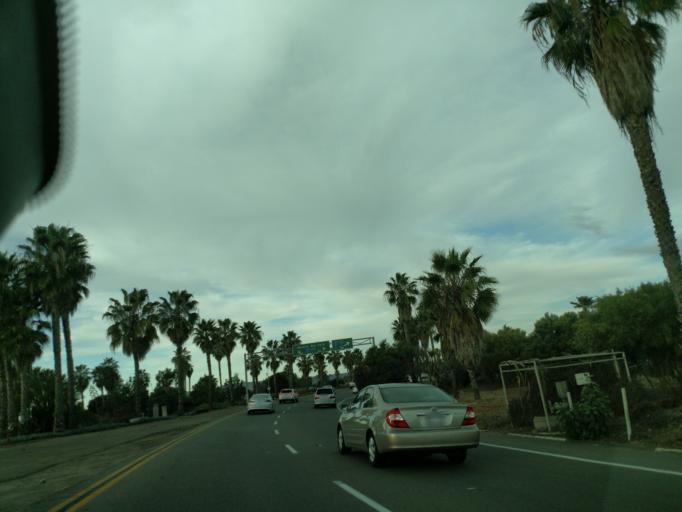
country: US
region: California
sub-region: San Diego County
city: Coronado
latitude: 32.7528
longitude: -117.2367
